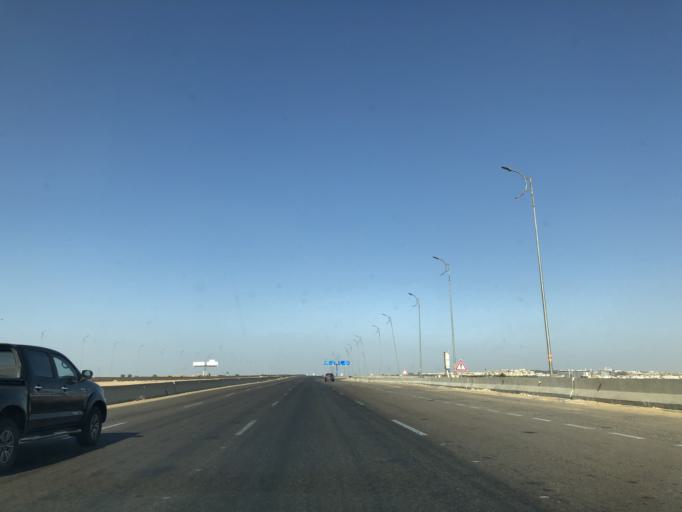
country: EG
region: Al Jizah
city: Awsim
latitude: 30.0730
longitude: 30.9193
